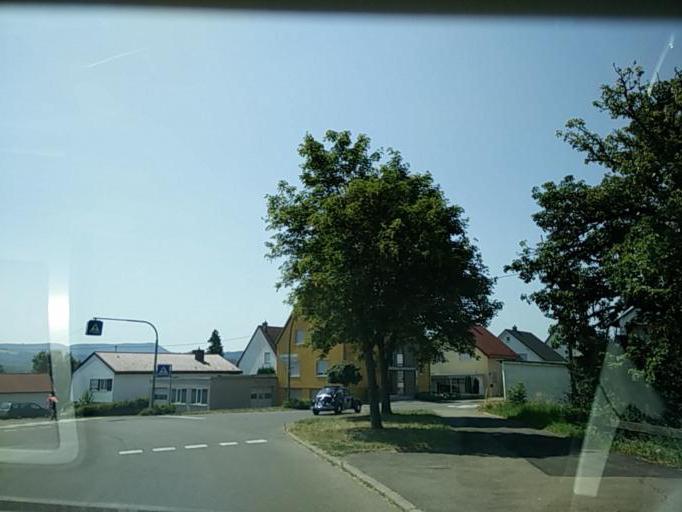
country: DE
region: Baden-Wuerttemberg
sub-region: Tuebingen Region
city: Gomaringen
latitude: 48.4573
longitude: 9.1021
